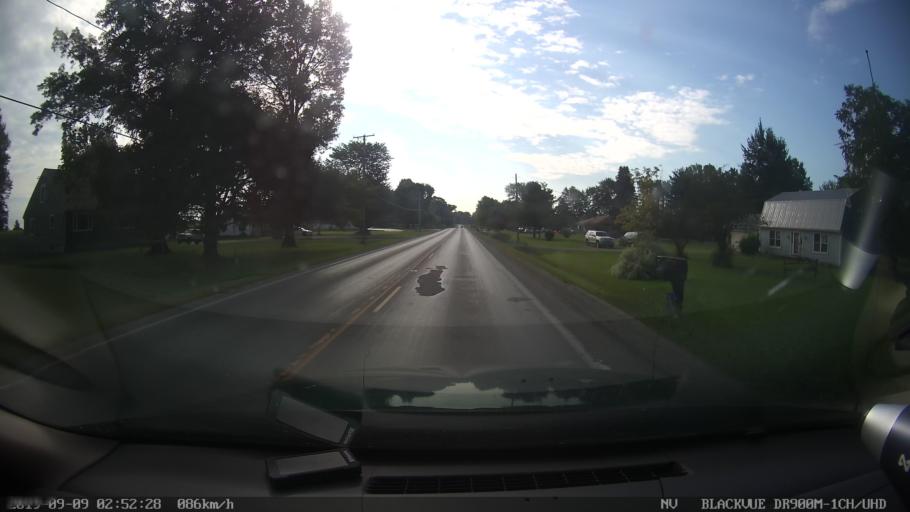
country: US
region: Ohio
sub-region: Crawford County
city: Galion
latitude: 40.7511
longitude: -82.8565
